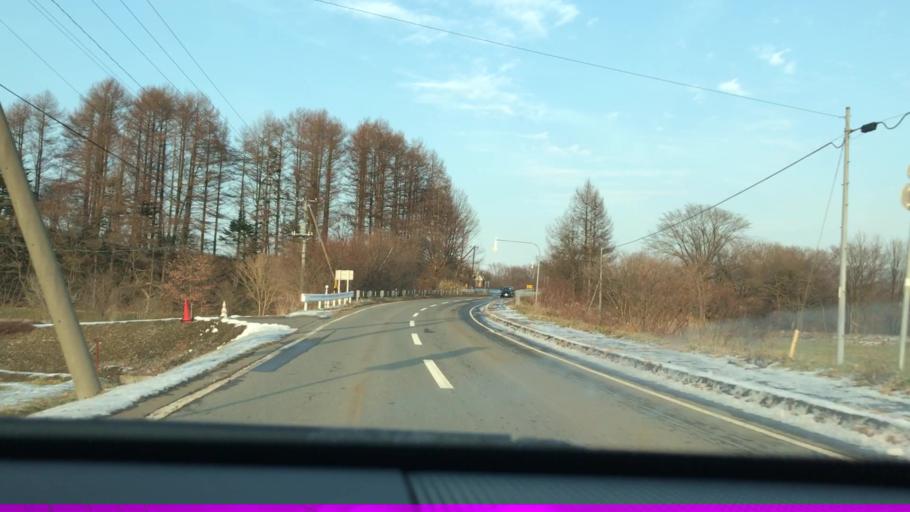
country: JP
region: Hokkaido
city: Shizunai-furukawacho
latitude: 42.4249
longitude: 142.4024
